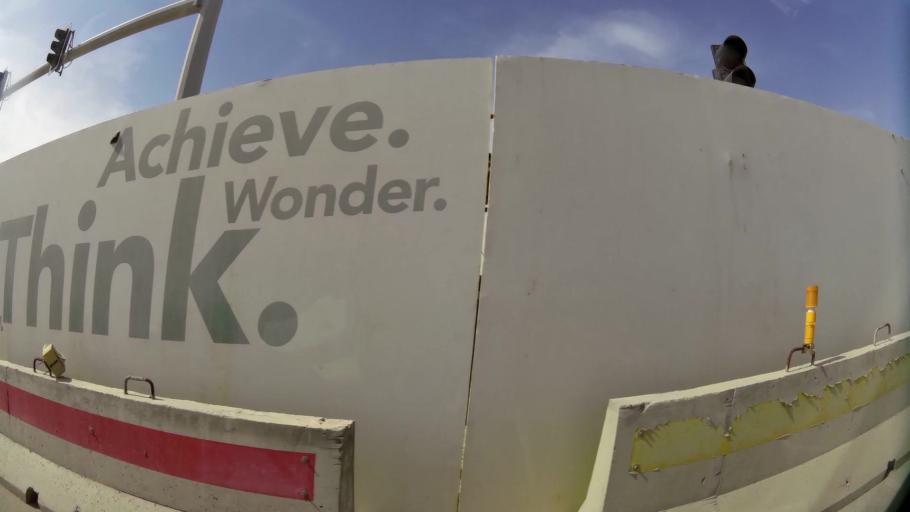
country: QA
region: Baladiyat ar Rayyan
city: Ar Rayyan
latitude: 25.3224
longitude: 51.4298
